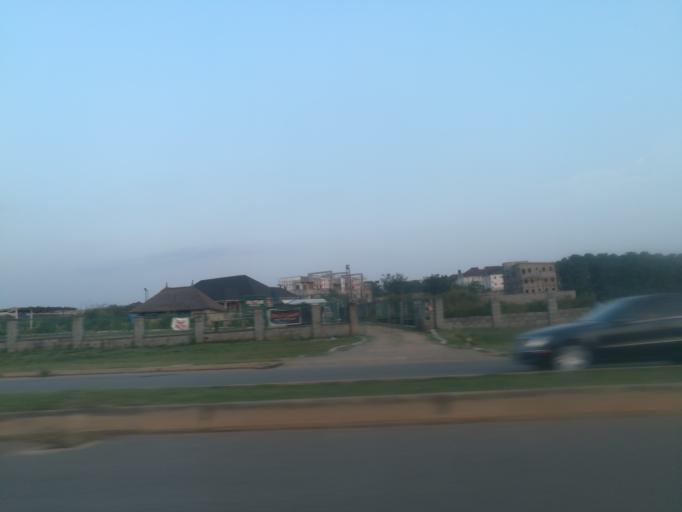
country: NG
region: Abuja Federal Capital Territory
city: Abuja
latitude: 9.0590
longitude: 7.4350
